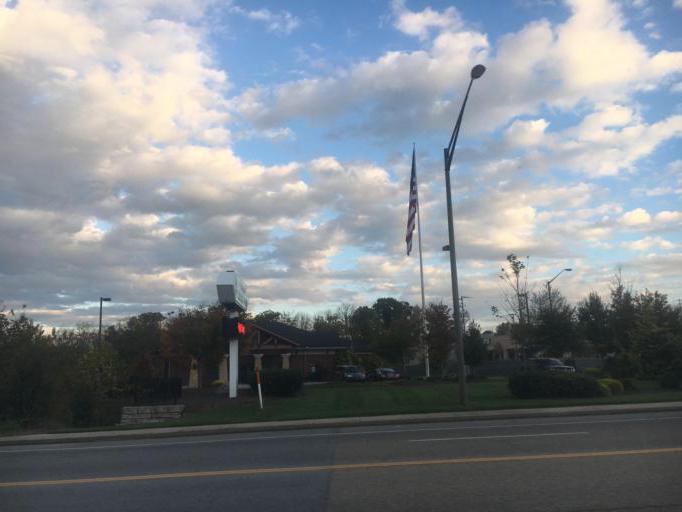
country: US
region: Tennessee
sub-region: Washington County
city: Gray
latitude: 36.4189
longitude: -82.4684
